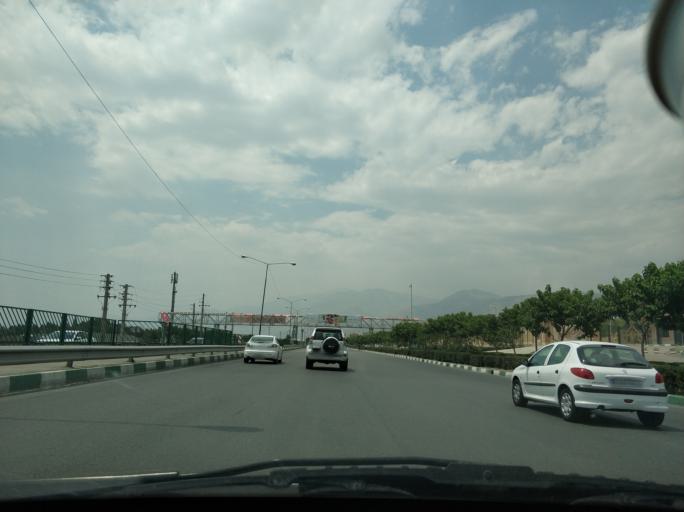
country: IR
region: Tehran
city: Tajrish
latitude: 35.7606
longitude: 51.5716
